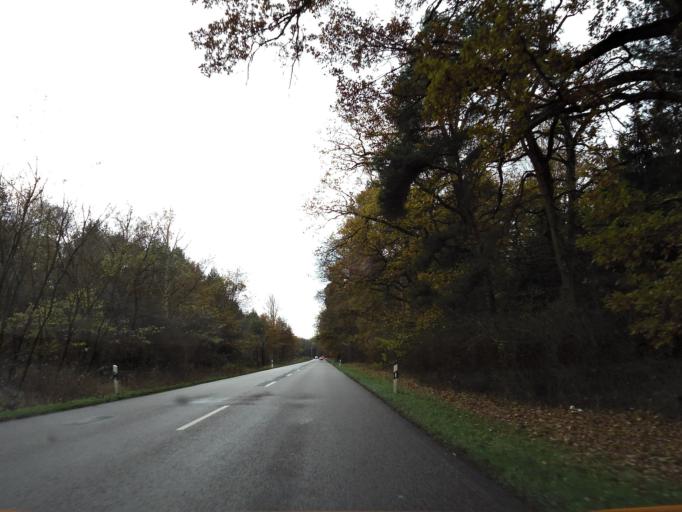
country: DE
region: Saxony-Anhalt
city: Haldensleben I
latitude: 52.3474
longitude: 11.4560
